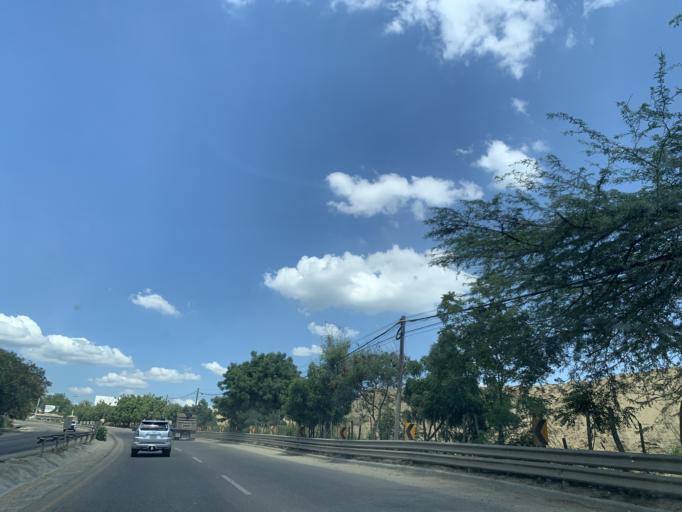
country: DO
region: Santiago
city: Villa Bisono
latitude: 19.5479
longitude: -70.8513
